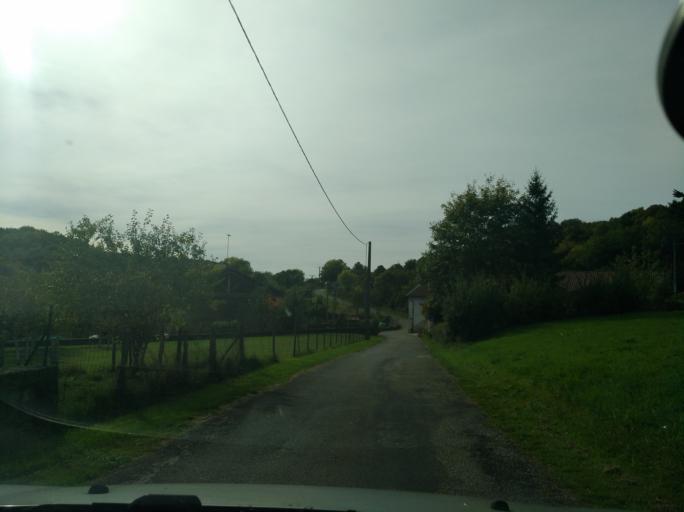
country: FR
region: Bourgogne
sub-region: Departement de Saone-et-Loire
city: Cuiseaux
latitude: 46.4582
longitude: 5.3864
